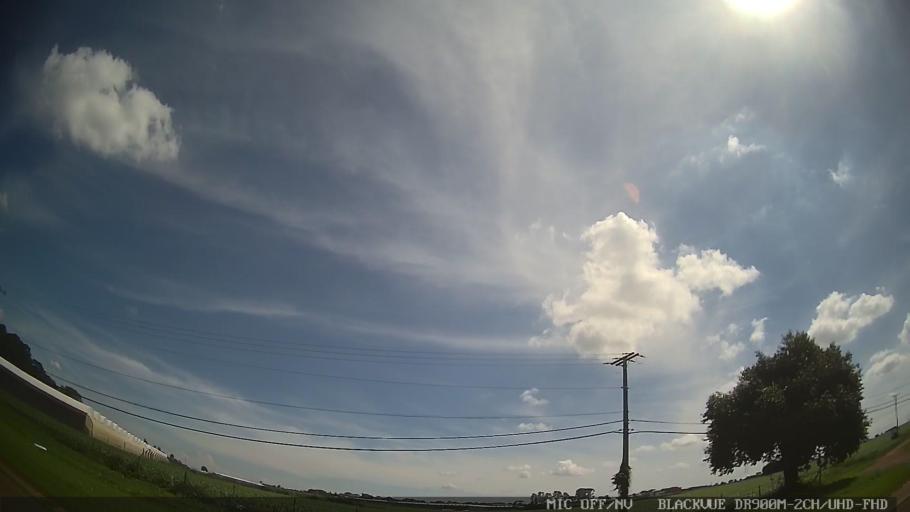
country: BR
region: Sao Paulo
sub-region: Artur Nogueira
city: Artur Nogueira
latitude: -22.6180
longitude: -47.0704
